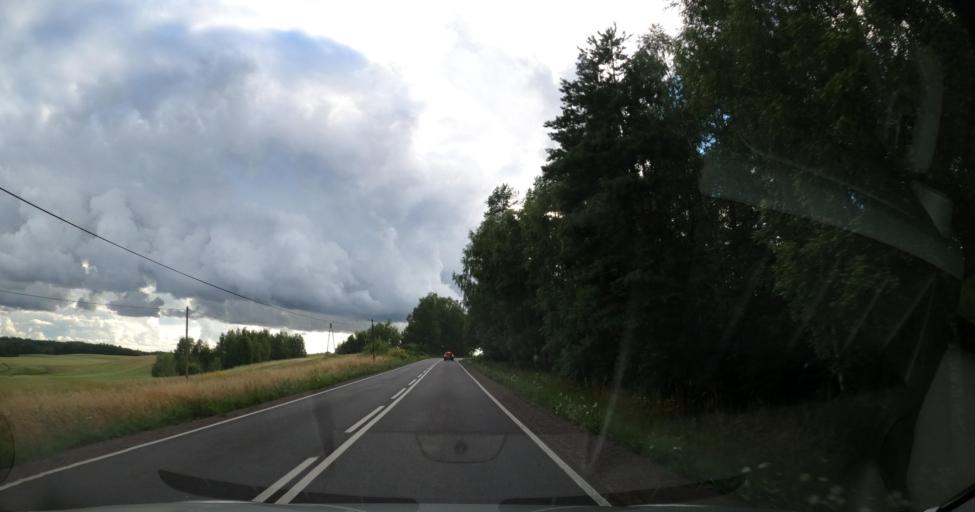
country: PL
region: Pomeranian Voivodeship
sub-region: Powiat bytowski
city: Czarna Dabrowka
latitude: 54.3457
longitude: 17.5882
